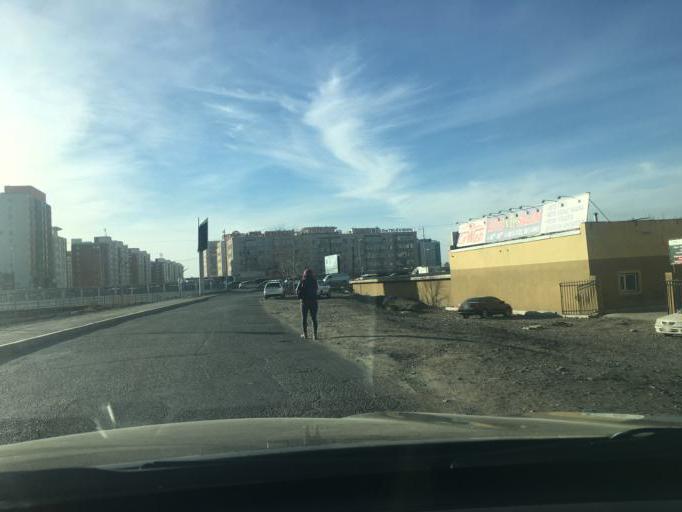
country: MN
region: Ulaanbaatar
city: Ulaanbaatar
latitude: 47.9024
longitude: 106.8945
